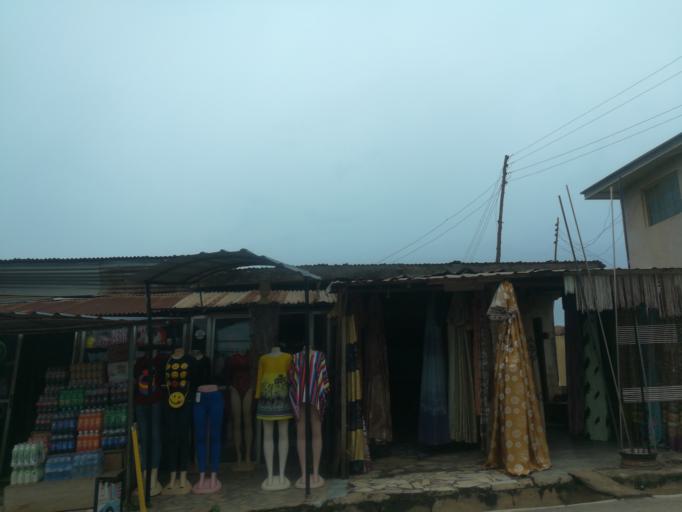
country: NG
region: Oyo
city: Ibadan
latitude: 7.3278
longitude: 3.8915
